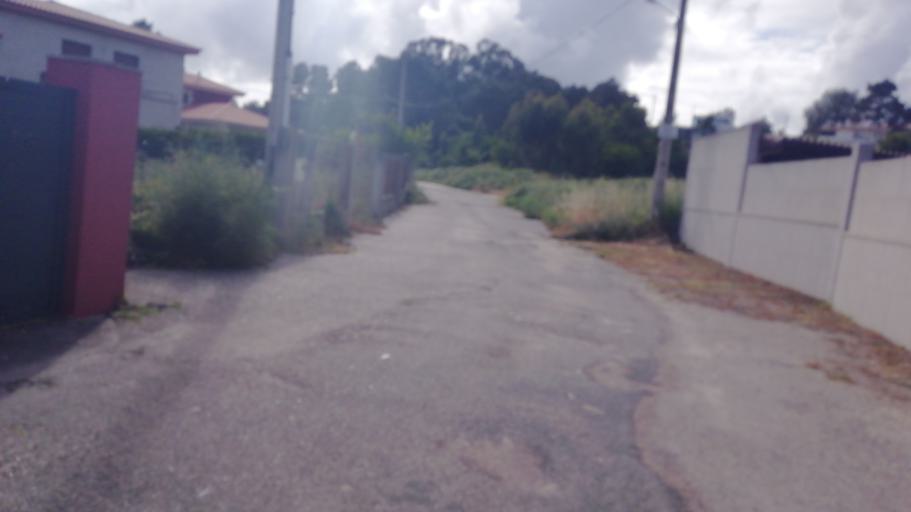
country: ES
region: Galicia
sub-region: Provincia de Pontevedra
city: A Guarda
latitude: 41.8756
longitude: -8.8702
